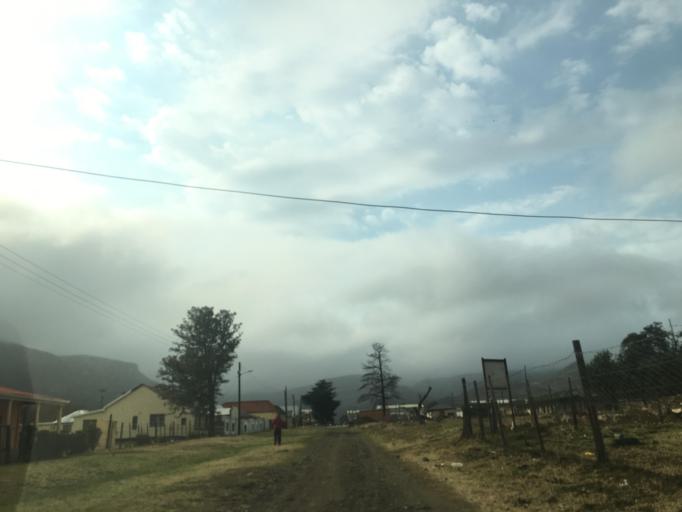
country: ZA
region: Eastern Cape
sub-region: Chris Hani District Municipality
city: Cala
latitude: -31.5225
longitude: 27.6926
